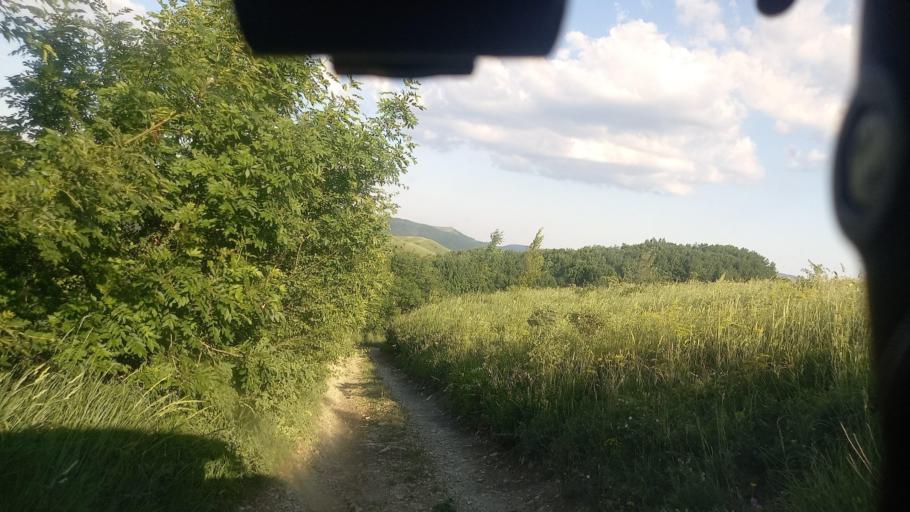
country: RU
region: Krasnodarskiy
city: Gelendzhik
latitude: 44.6179
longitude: 38.1942
